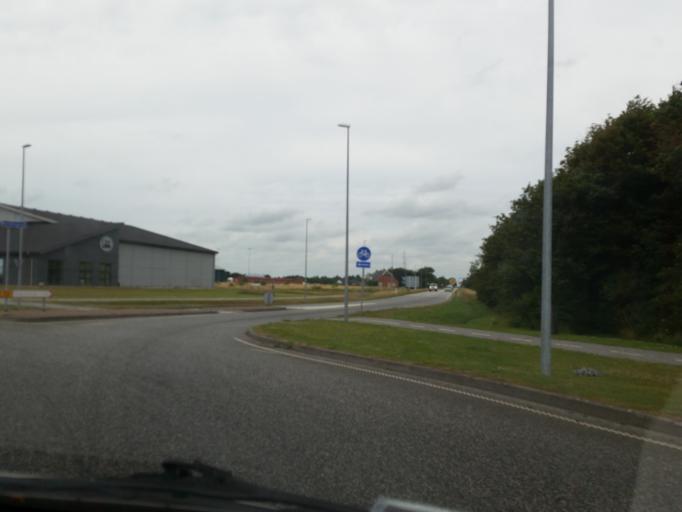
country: DK
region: South Denmark
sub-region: Esbjerg Kommune
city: Ribe
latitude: 55.3518
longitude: 8.7836
